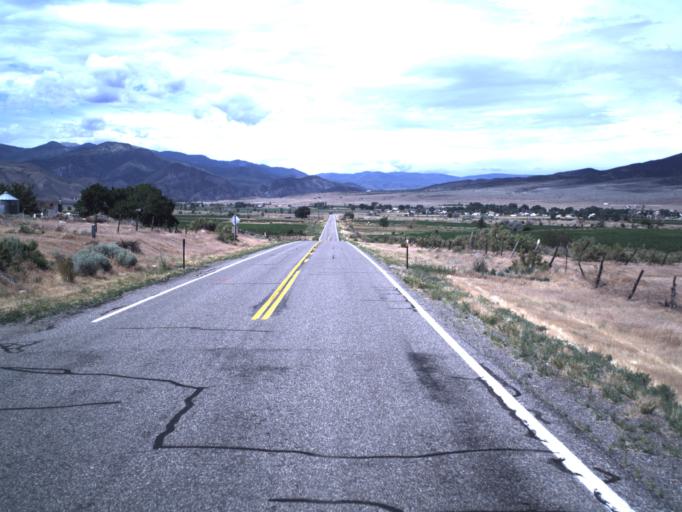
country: US
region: Utah
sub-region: Sevier County
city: Monroe
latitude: 38.6326
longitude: -112.1901
